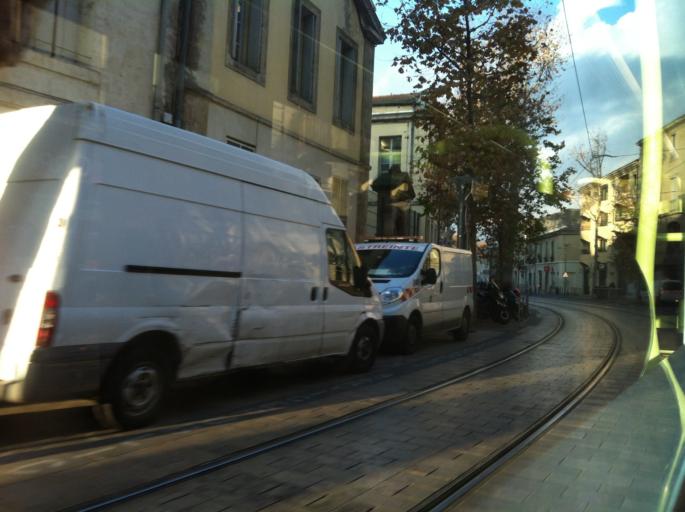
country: FR
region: Languedoc-Roussillon
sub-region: Departement de l'Herault
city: Montpellier
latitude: 43.6145
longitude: 3.8800
